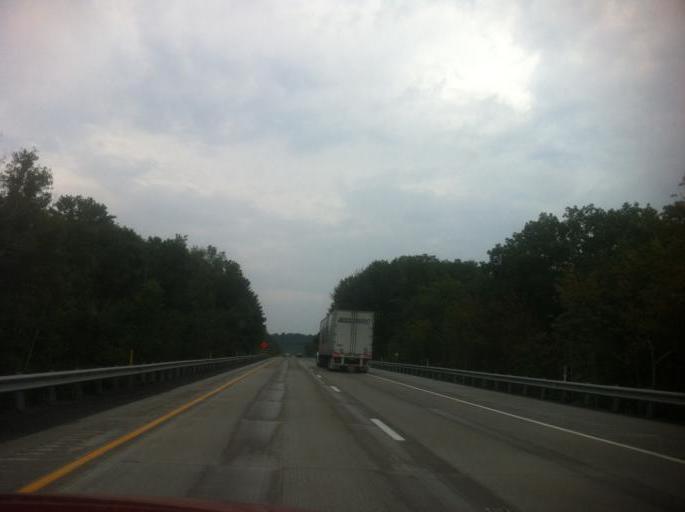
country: US
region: Pennsylvania
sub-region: Jefferson County
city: Falls Creek
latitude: 41.1545
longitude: -78.8405
